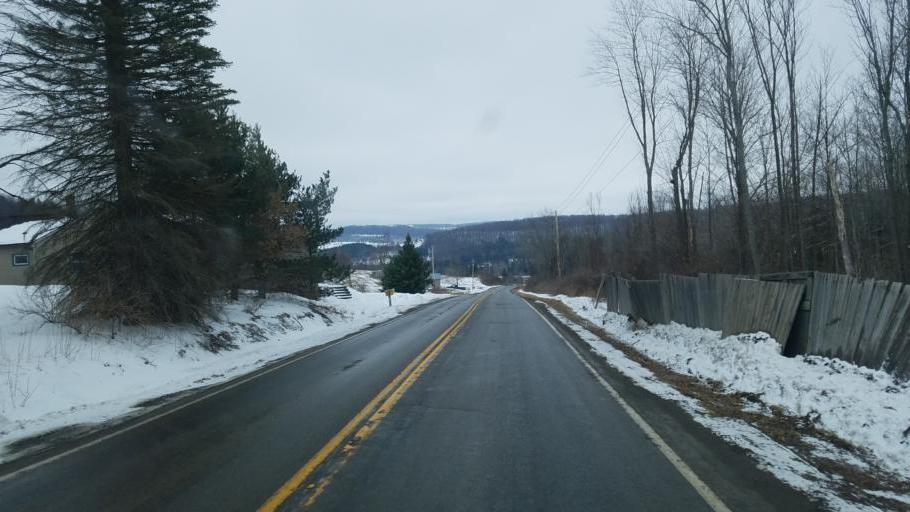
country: US
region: Pennsylvania
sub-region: Tioga County
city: Elkland
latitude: 42.0970
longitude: -77.4136
